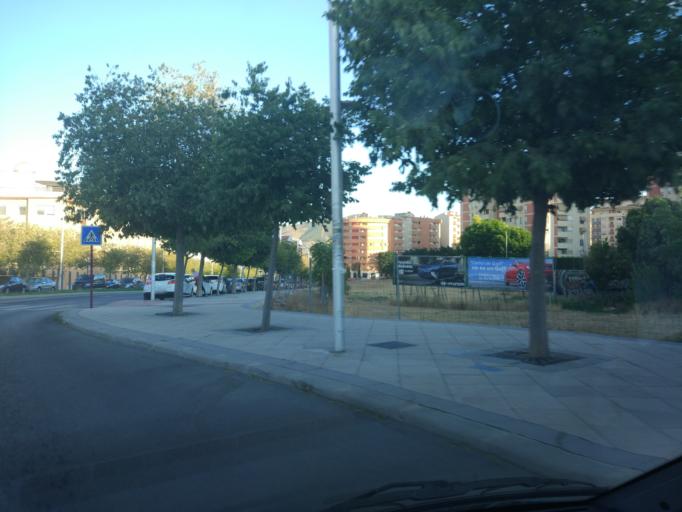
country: ES
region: Andalusia
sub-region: Provincia de Jaen
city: Jaen
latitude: 37.7876
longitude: -3.7793
